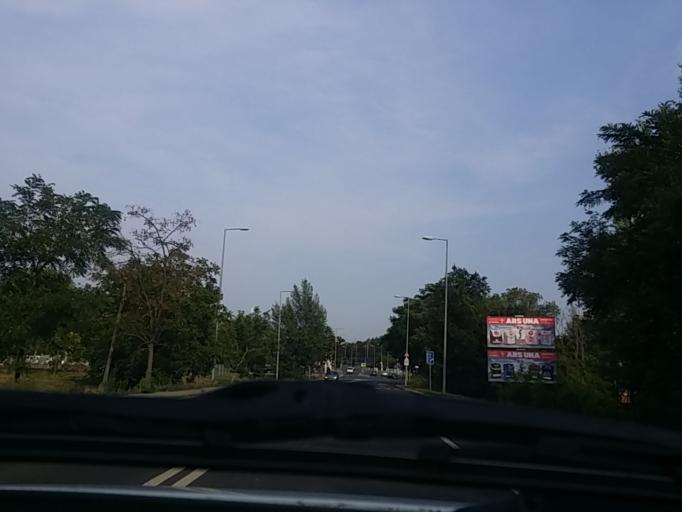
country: HU
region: Budapest
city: Budapest XII. keruelet
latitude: 47.4617
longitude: 18.9965
